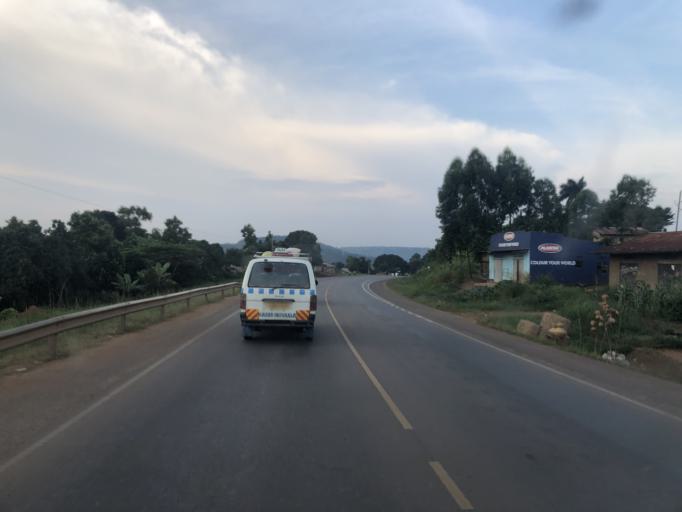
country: UG
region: Central Region
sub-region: Mpigi District
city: Mpigi
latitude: 0.2385
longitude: 32.3487
